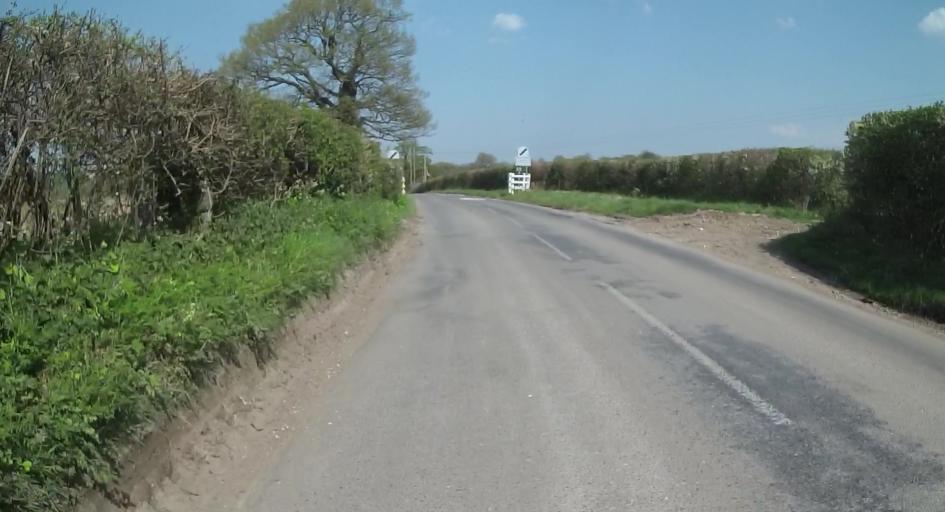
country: GB
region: England
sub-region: Hampshire
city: Basingstoke
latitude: 51.2981
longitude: -1.0993
